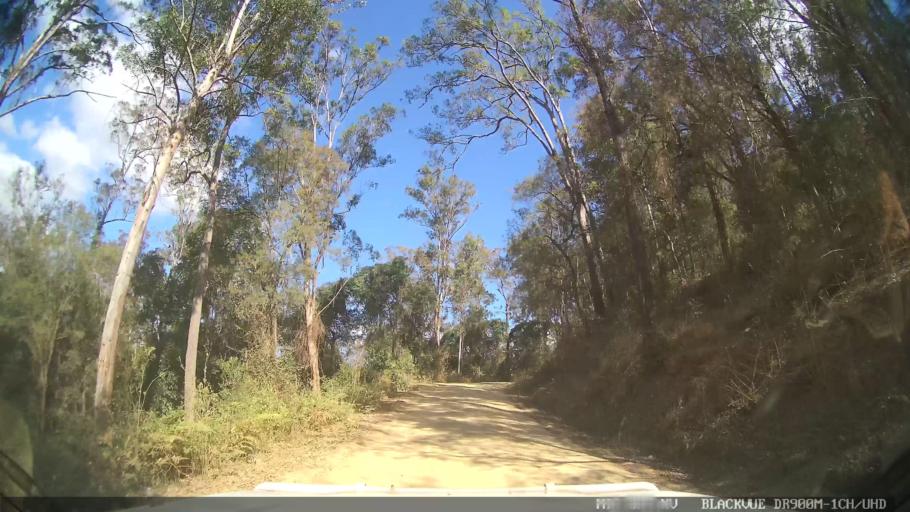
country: AU
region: Queensland
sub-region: Moreton Bay
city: Woodford
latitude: -26.6683
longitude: 152.6355
